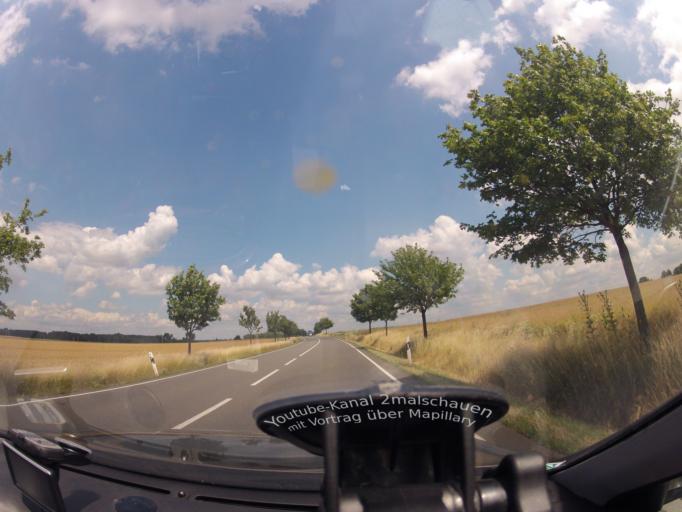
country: DE
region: Saxony
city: Doberschutz
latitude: 51.4774
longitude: 12.7182
